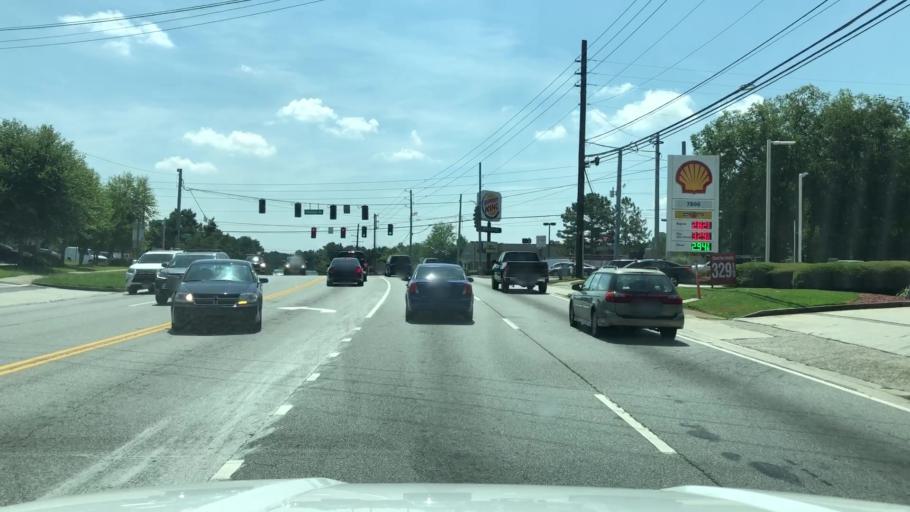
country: US
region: Georgia
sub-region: Gwinnett County
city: Norcross
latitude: 33.9687
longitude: -84.2588
